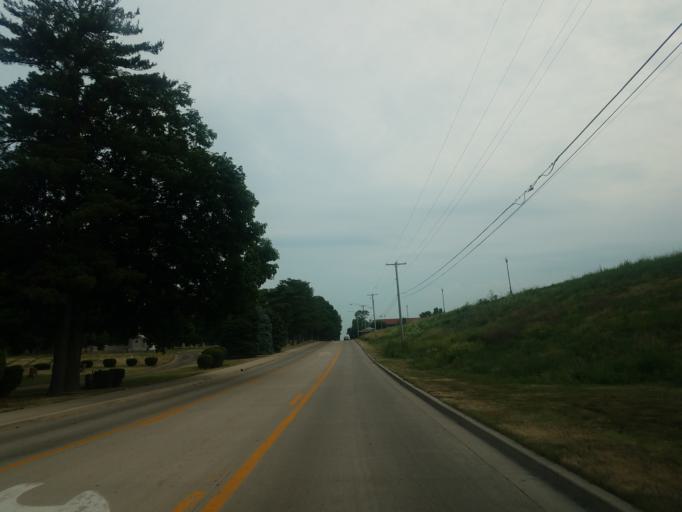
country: US
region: Illinois
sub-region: McLean County
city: Bloomington
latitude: 40.4650
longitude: -89.0065
